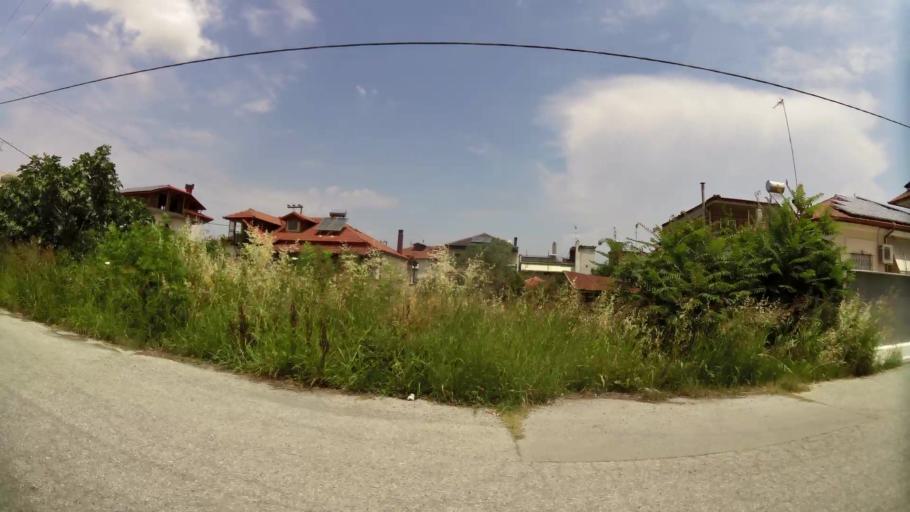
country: GR
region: Central Macedonia
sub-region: Nomos Pierias
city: Peristasi
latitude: 40.2707
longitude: 22.5417
